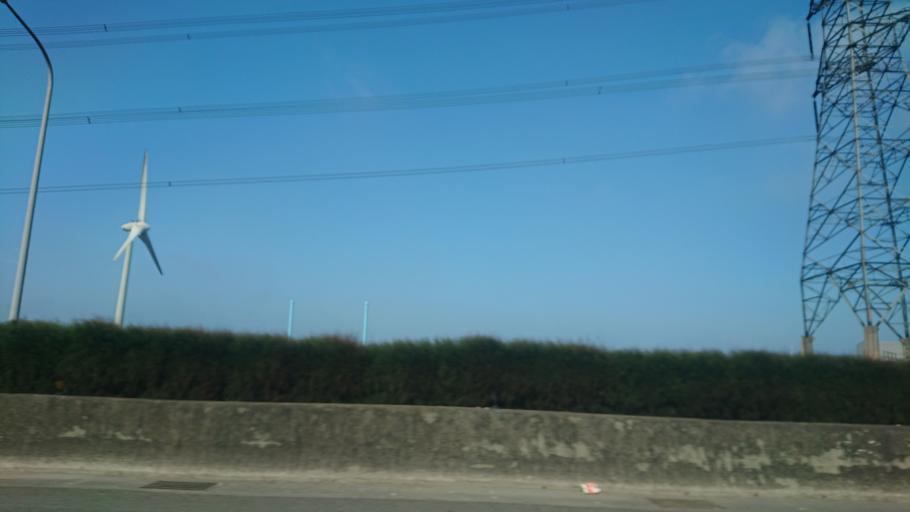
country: TW
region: Taiwan
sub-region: Changhua
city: Chang-hua
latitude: 24.1471
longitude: 120.4509
